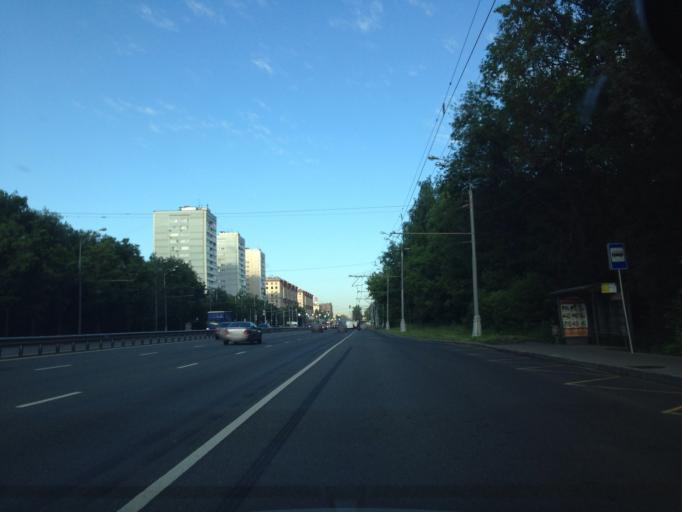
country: RU
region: Moskovskaya
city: Izmaylovo
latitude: 55.7667
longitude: 37.7938
